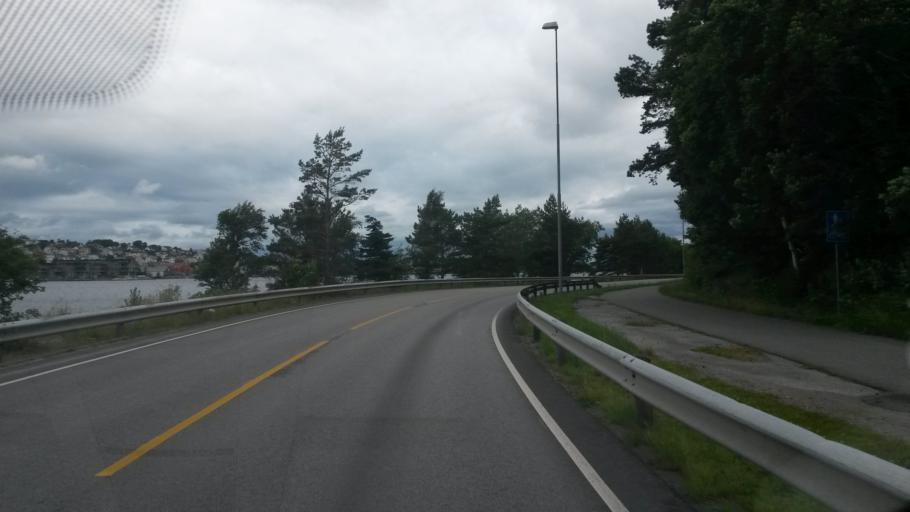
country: NO
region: Rogaland
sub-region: Sandnes
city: Sandnes
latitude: 58.8602
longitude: 5.7541
